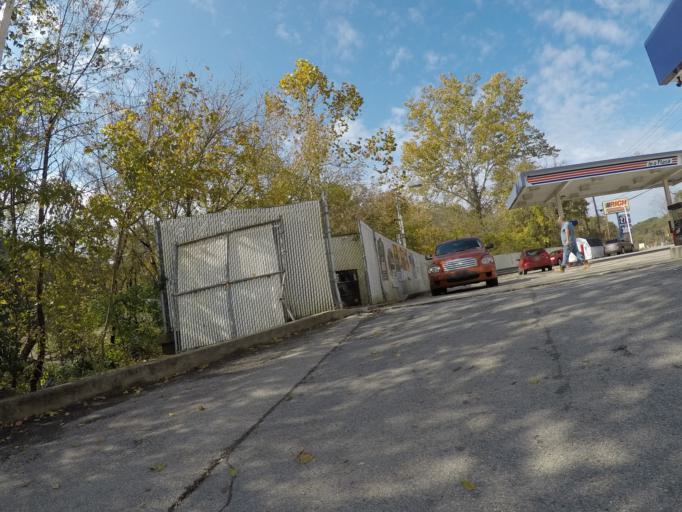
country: US
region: West Virginia
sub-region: Cabell County
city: Pea Ridge
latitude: 38.3833
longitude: -82.3766
